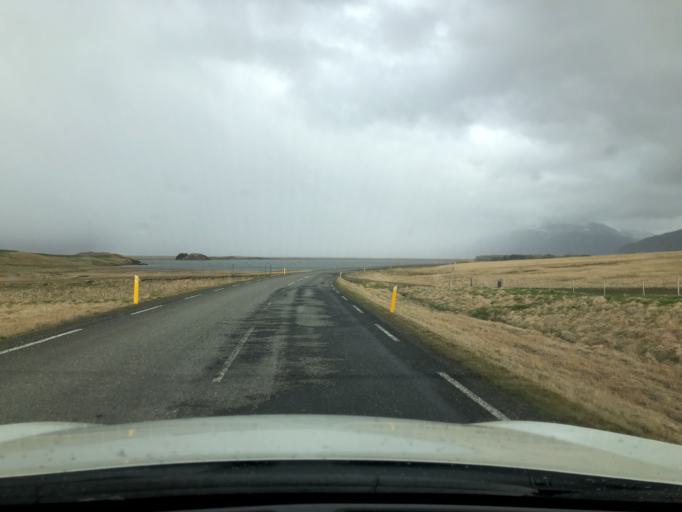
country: IS
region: East
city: Hoefn
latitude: 64.3302
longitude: -15.2401
